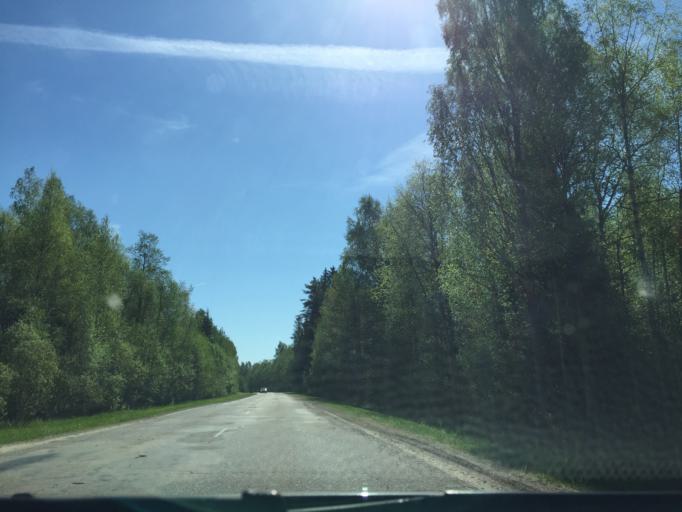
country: LV
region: Incukalns
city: Incukalns
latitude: 57.0255
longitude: 24.7506
